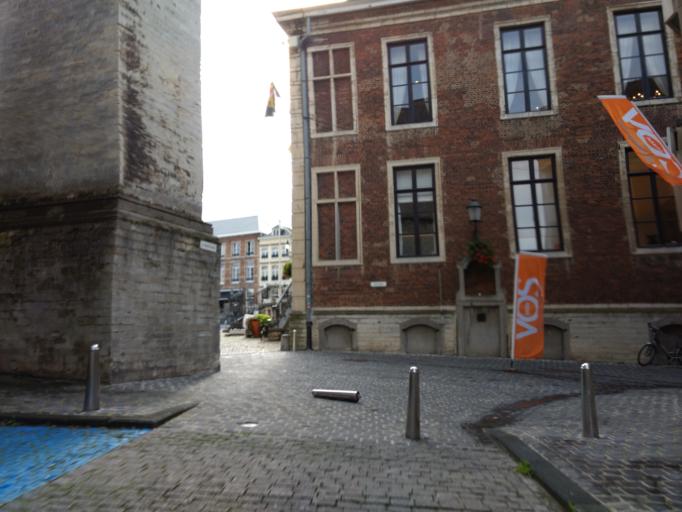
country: BE
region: Flanders
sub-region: Provincie Vlaams-Brabant
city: Diest
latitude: 50.9849
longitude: 5.0505
